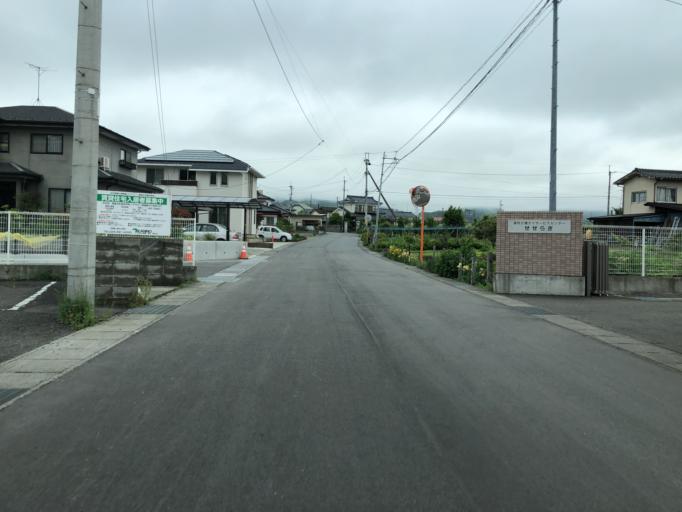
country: JP
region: Fukushima
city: Fukushima-shi
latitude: 37.7691
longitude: 140.3935
